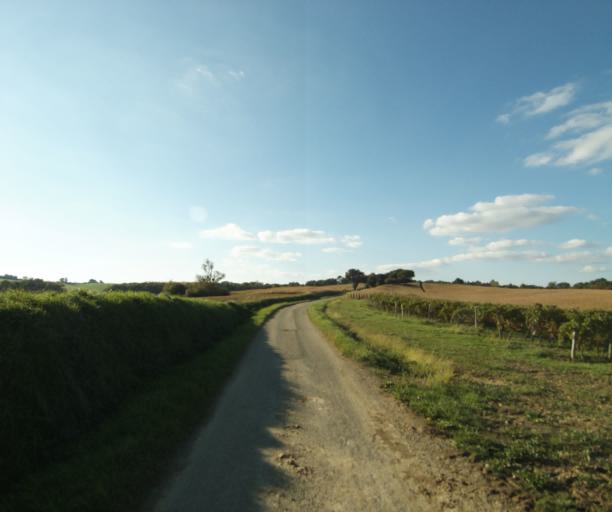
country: FR
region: Midi-Pyrenees
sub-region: Departement du Gers
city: Eauze
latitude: 43.7643
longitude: 0.1431
